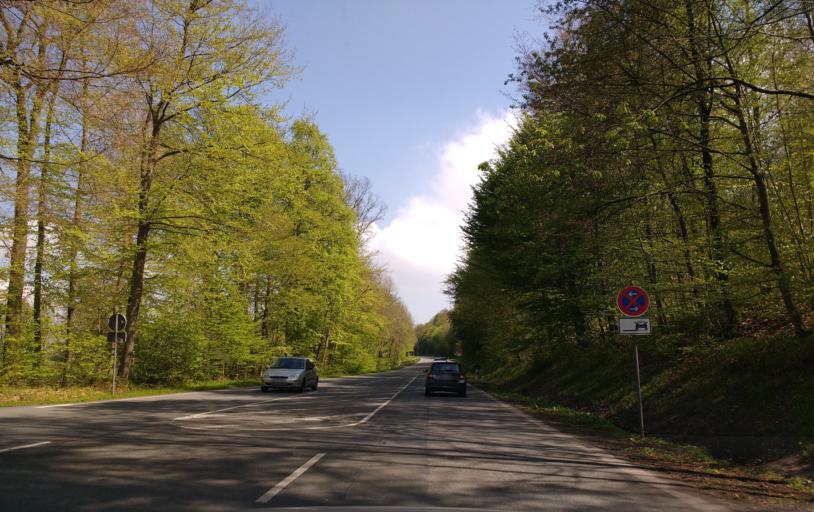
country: DE
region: North Rhine-Westphalia
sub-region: Regierungsbezirk Detmold
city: Schieder-Schwalenberg
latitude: 51.9189
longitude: 9.1651
